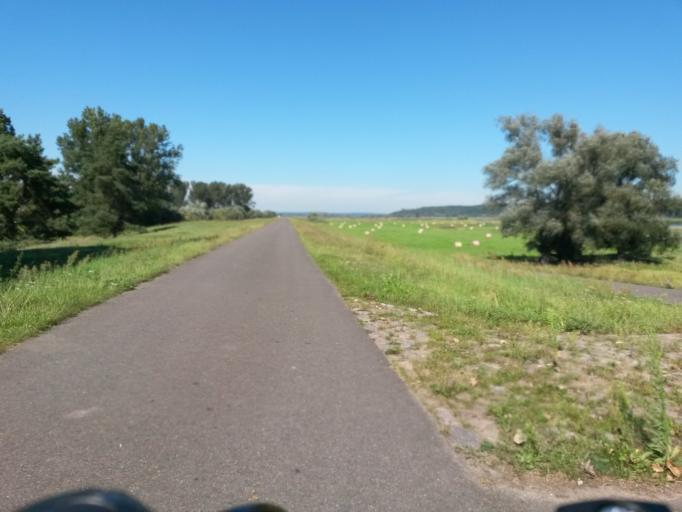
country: PL
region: West Pomeranian Voivodeship
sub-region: Powiat gryfinski
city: Cedynia
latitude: 52.9054
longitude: 14.1474
